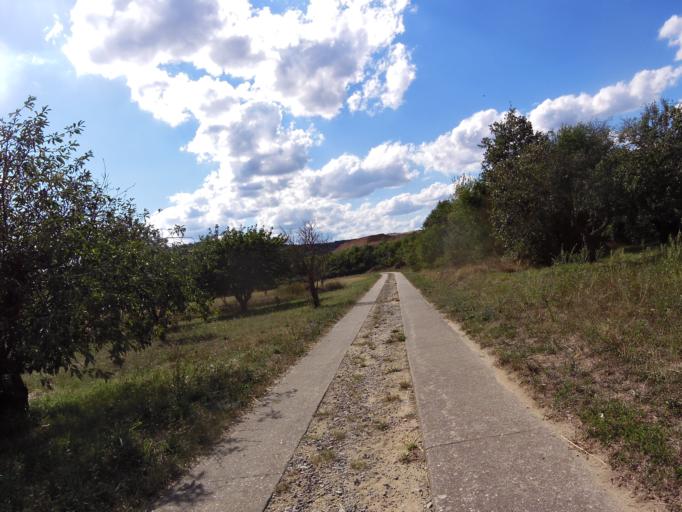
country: DE
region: Bavaria
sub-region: Regierungsbezirk Unterfranken
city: Eibelstadt
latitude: 49.7377
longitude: 9.9982
